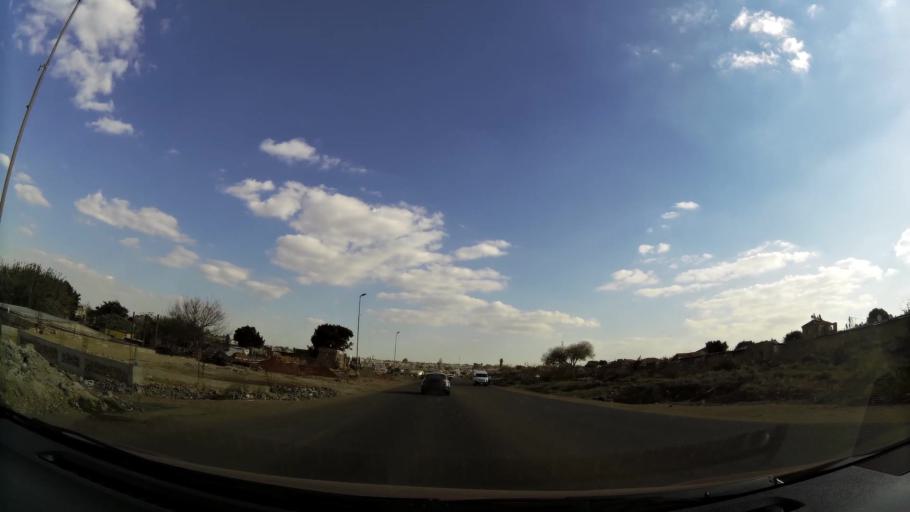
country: ZA
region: Gauteng
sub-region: Ekurhuleni Metropolitan Municipality
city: Tembisa
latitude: -26.0002
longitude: 28.1837
